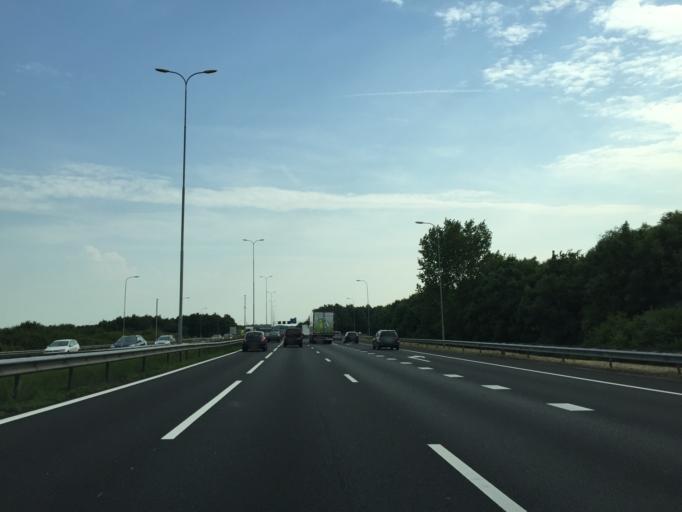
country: NL
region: Utrecht
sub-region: Gemeente Vianen
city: Vianen
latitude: 51.9959
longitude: 5.1123
